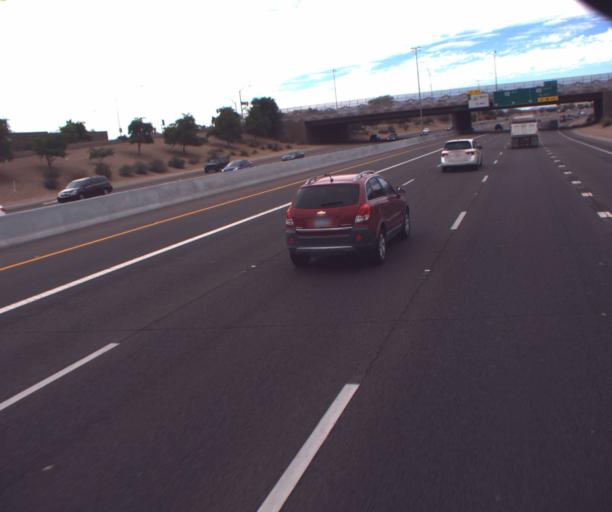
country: US
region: Arizona
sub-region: Maricopa County
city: Chandler
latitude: 33.2873
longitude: -111.8745
